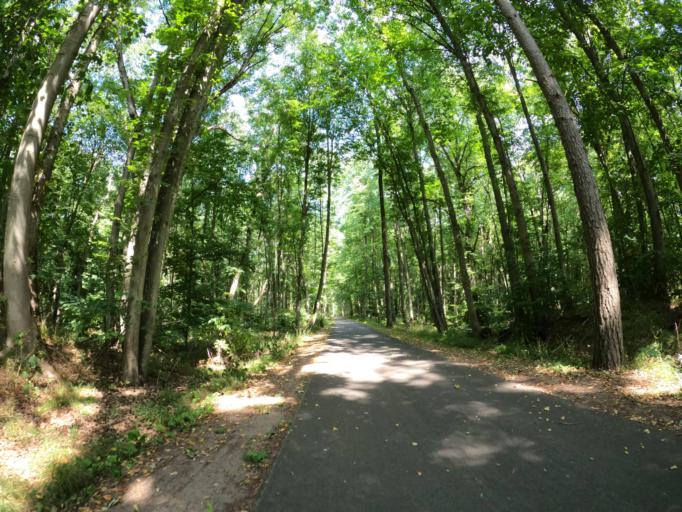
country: DE
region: Mecklenburg-Vorpommern
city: Woldegk
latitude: 53.3142
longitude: 13.5782
